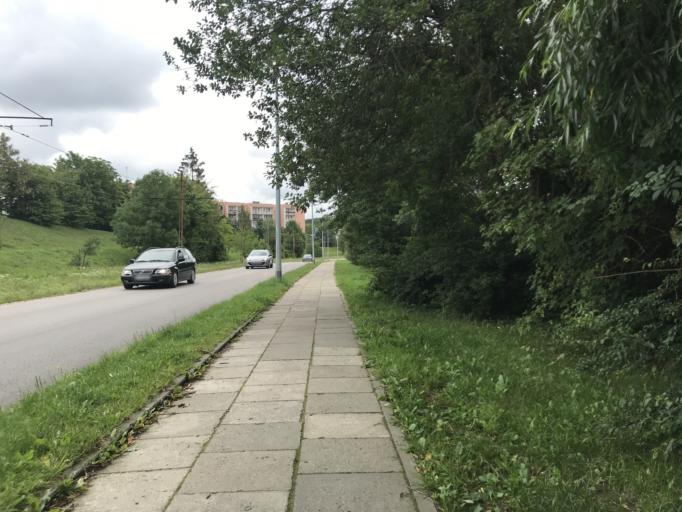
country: PL
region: Warmian-Masurian Voivodeship
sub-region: Powiat elblaski
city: Elblag
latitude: 54.1776
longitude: 19.4283
